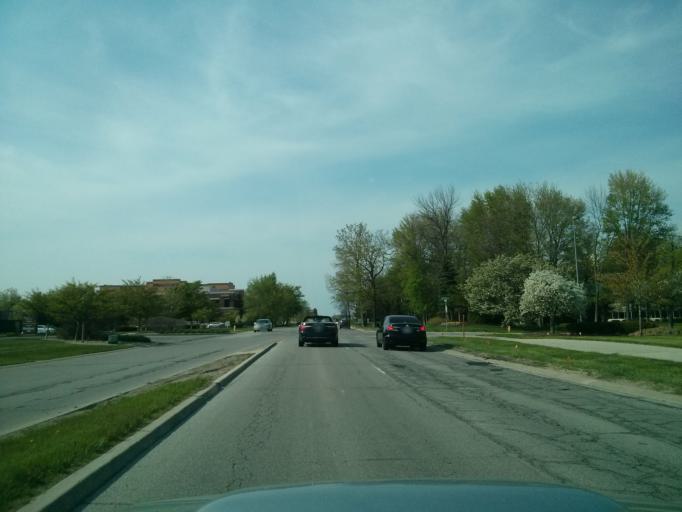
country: US
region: Indiana
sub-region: Hamilton County
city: Carmel
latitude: 39.9606
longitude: -86.1549
